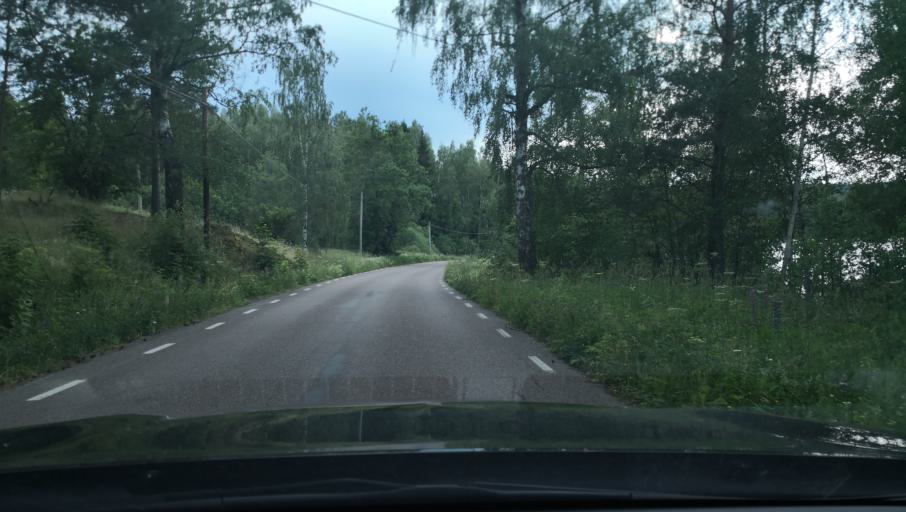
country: SE
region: Dalarna
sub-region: Smedjebackens Kommun
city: Smedjebacken
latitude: 60.0474
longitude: 15.5226
